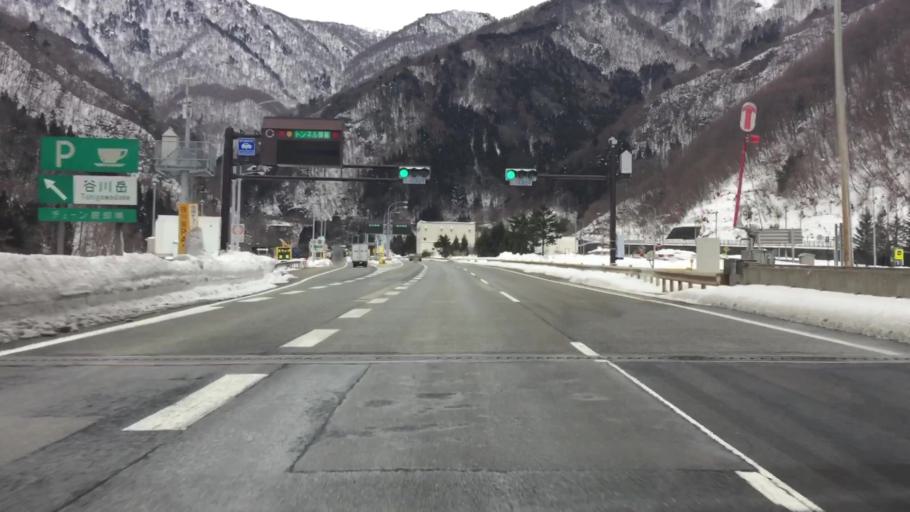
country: JP
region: Gunma
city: Numata
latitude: 36.7766
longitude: 138.9454
